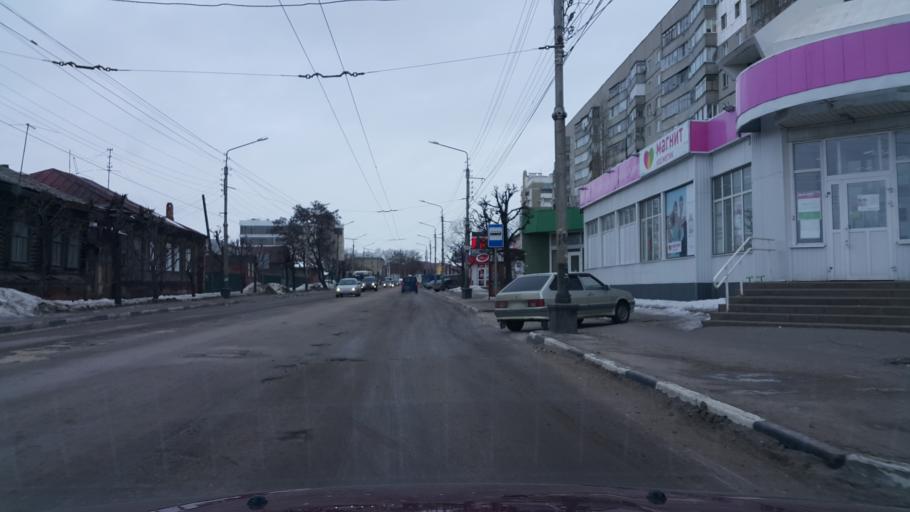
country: RU
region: Tambov
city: Tambov
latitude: 52.7328
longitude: 41.4420
